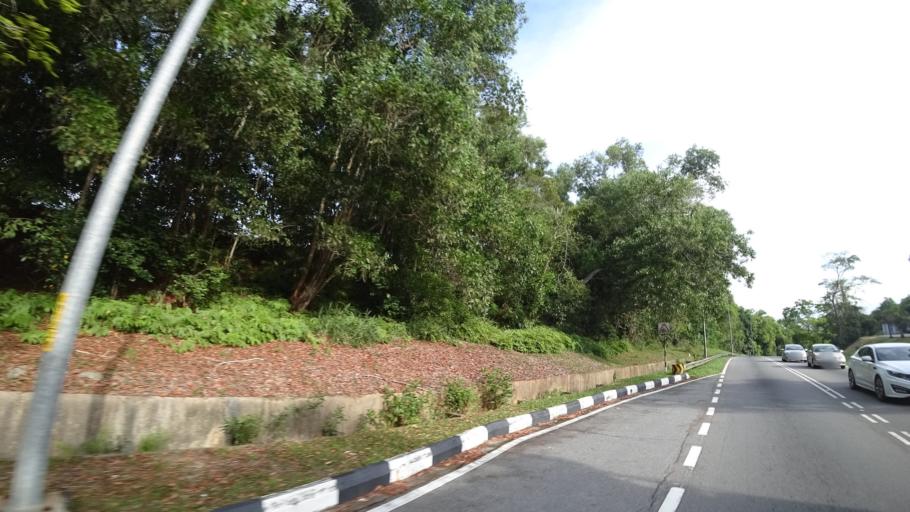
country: BN
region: Brunei and Muara
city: Bandar Seri Begawan
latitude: 4.8688
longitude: 114.9010
